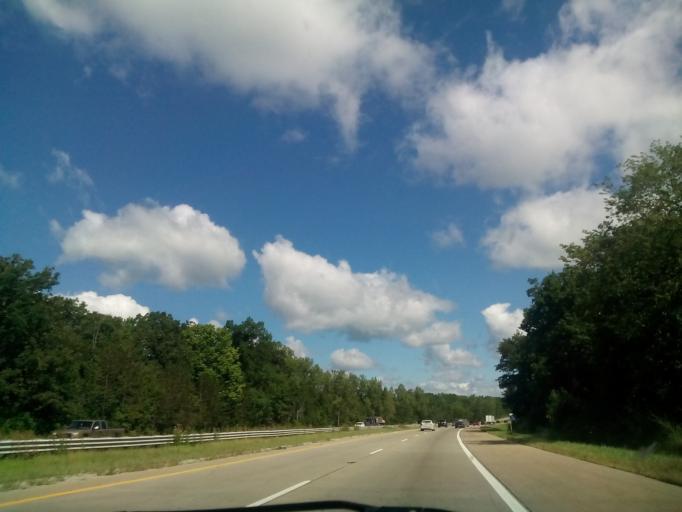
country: US
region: Michigan
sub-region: Genesee County
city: Lake Fenton
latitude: 42.8471
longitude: -83.7390
